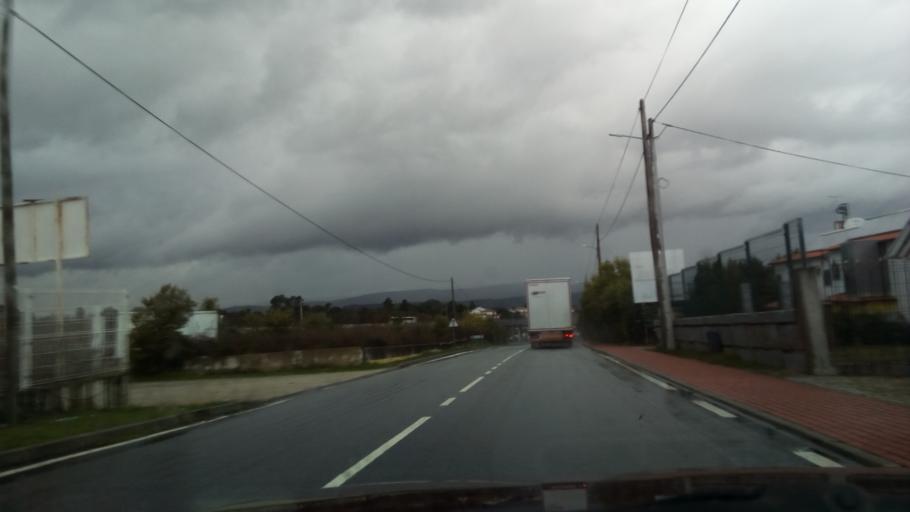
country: PT
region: Guarda
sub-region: Celorico da Beira
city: Celorico da Beira
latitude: 40.6346
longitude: -7.3486
